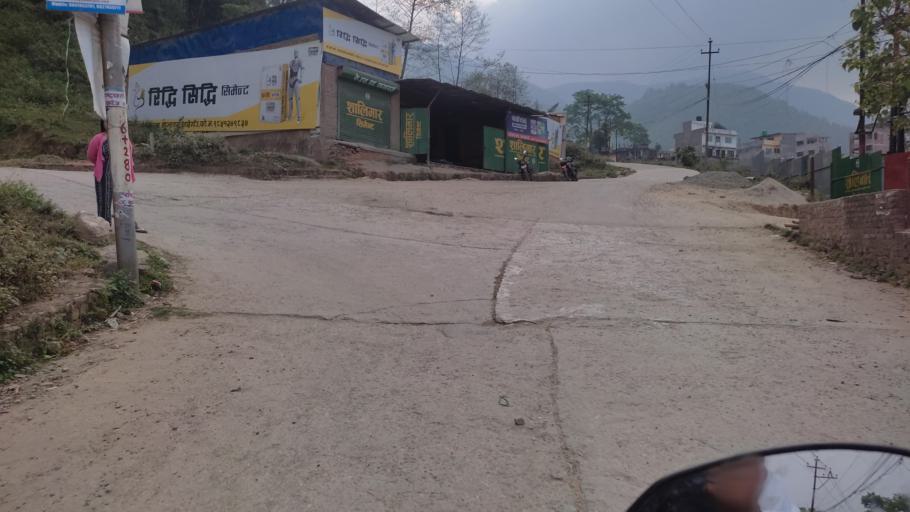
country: NP
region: Central Region
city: Kirtipur
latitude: 27.6683
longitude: 85.2456
